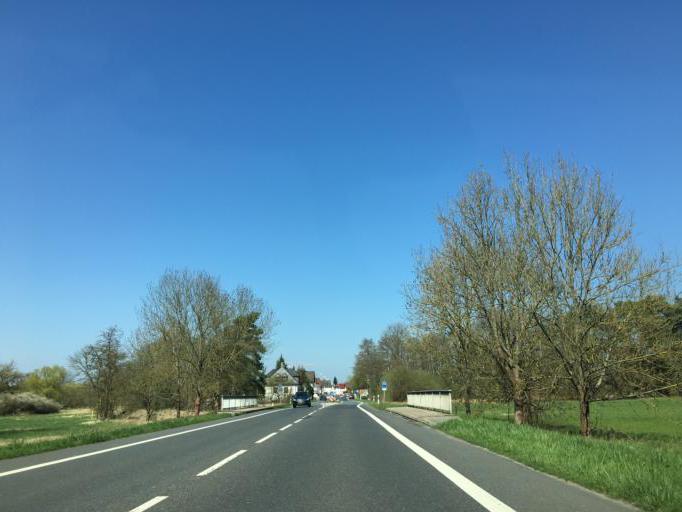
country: DE
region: Hesse
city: Obertshausen
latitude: 50.0909
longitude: 8.8623
